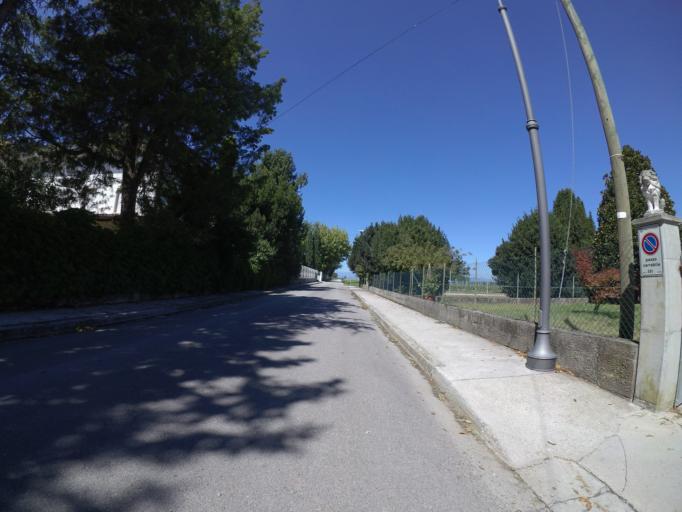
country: IT
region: Friuli Venezia Giulia
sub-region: Provincia di Udine
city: Rivignano
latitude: 45.8606
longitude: 13.0145
